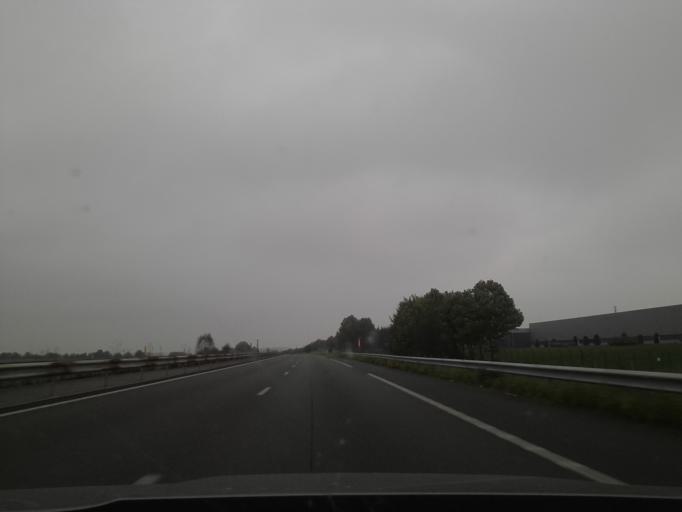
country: FR
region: Nord-Pas-de-Calais
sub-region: Departement du Nord
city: Neuville-Saint-Remy
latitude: 50.1932
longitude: 3.2016
